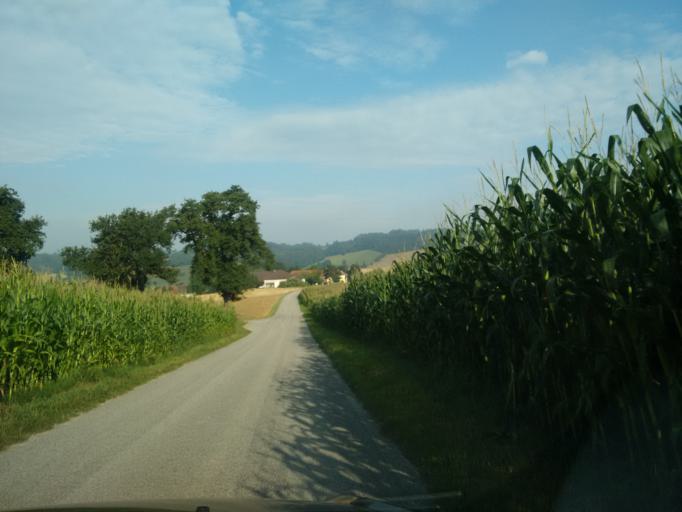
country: AT
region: Upper Austria
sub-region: Politischer Bezirk Grieskirchen
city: Bad Schallerbach
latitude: 48.2130
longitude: 13.9400
